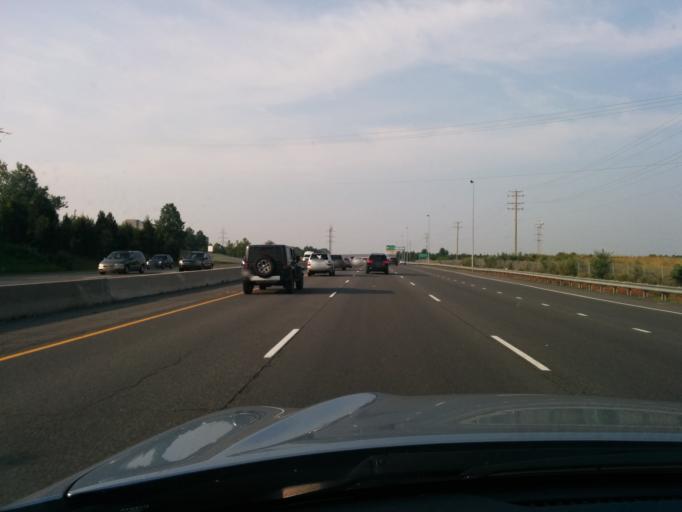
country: US
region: Virginia
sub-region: Loudoun County
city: Sterling
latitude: 39.0163
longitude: -77.4325
